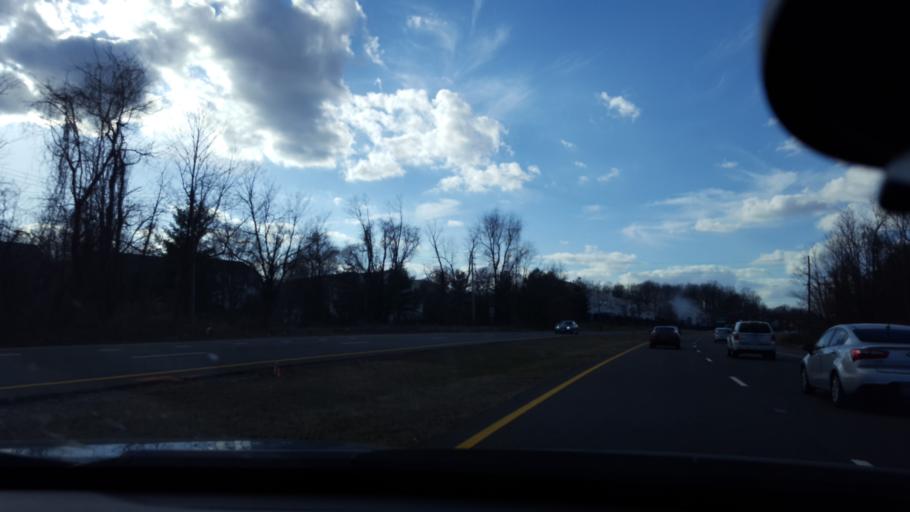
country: US
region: Maryland
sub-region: Prince George's County
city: Bowie
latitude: 38.9429
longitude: -76.7195
